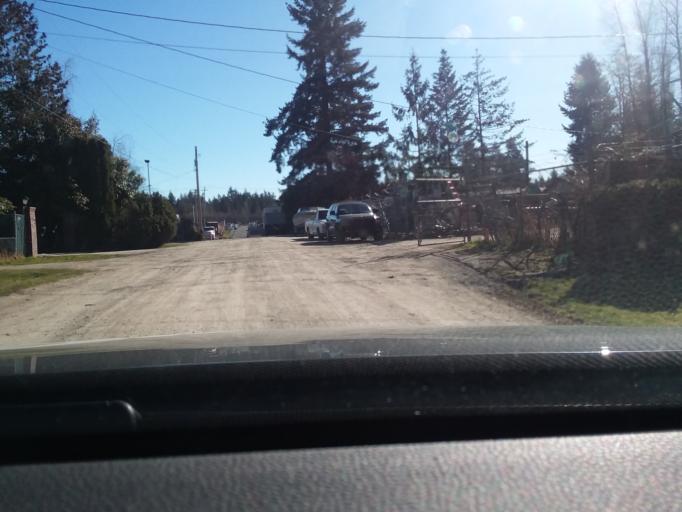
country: US
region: Washington
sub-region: Pierce County
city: Summit
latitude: 47.1367
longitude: -122.3600
